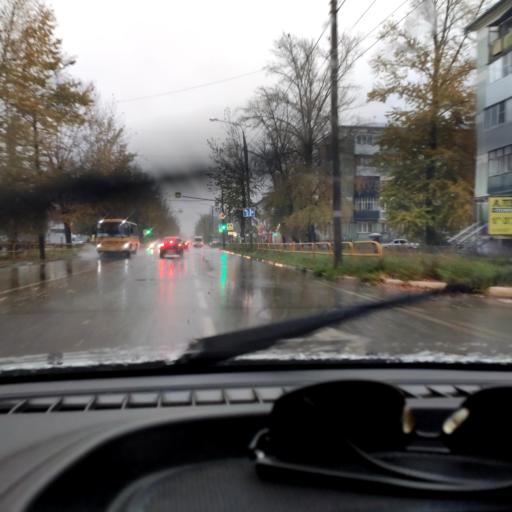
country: RU
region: Samara
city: Tol'yatti
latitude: 53.5338
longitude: 49.4110
